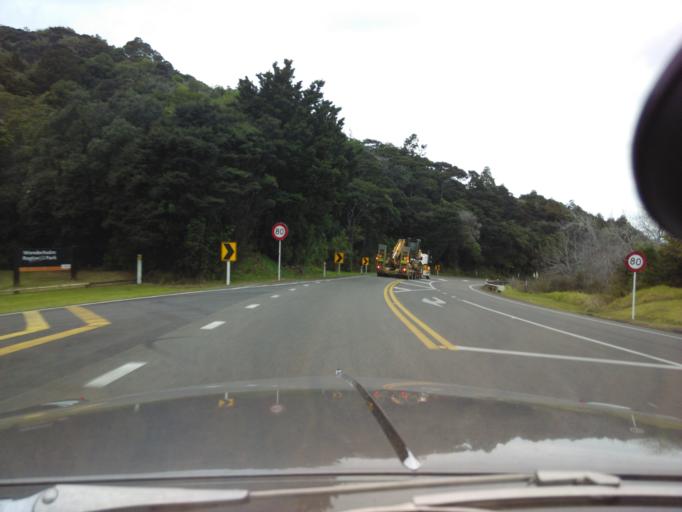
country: NZ
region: Auckland
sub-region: Auckland
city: Warkworth
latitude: -36.5377
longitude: 174.7036
